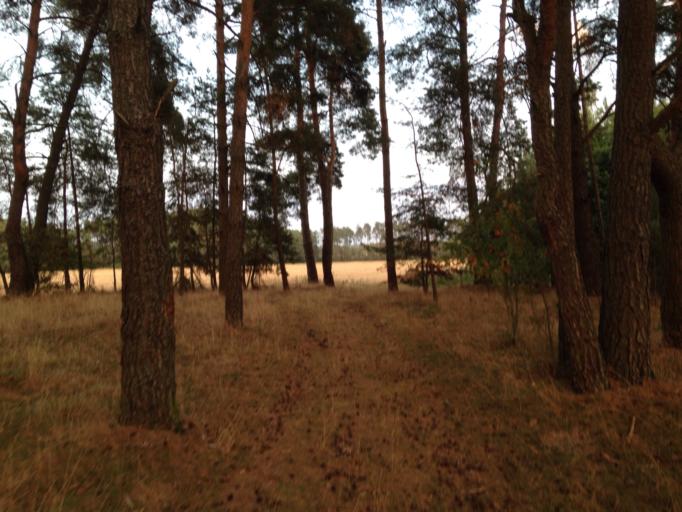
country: DE
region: Bavaria
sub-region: Regierungsbezirk Mittelfranken
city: Hilpoltstein
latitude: 49.1650
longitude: 11.1717
